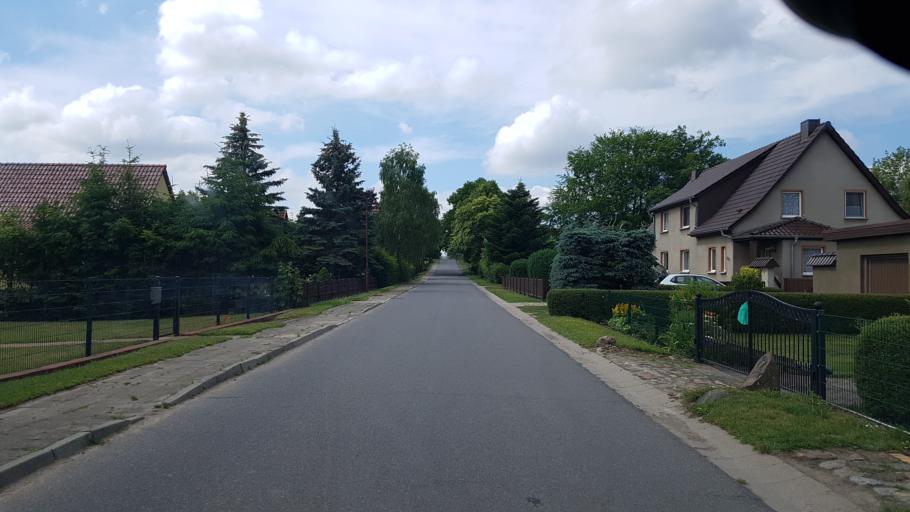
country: DE
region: Mecklenburg-Vorpommern
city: Strasburg
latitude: 53.4313
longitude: 13.7019
